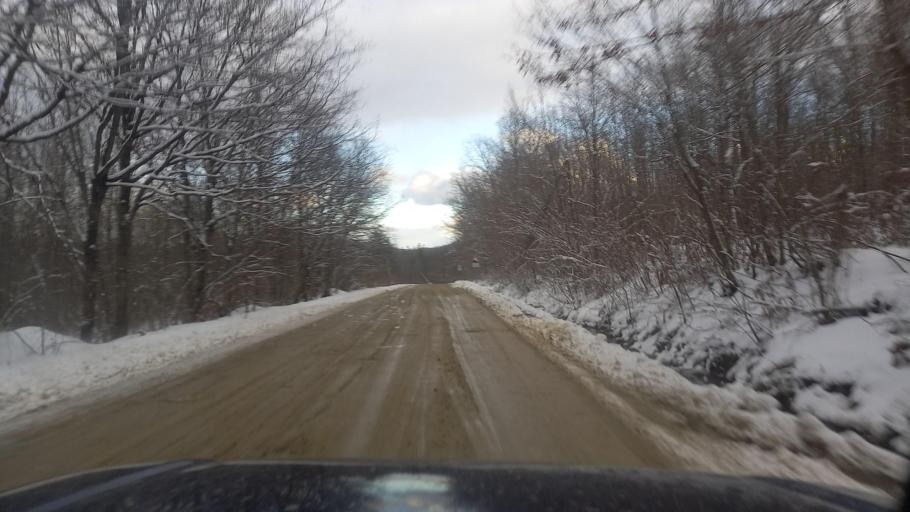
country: RU
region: Krasnodarskiy
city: Smolenskaya
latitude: 44.6754
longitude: 38.7380
